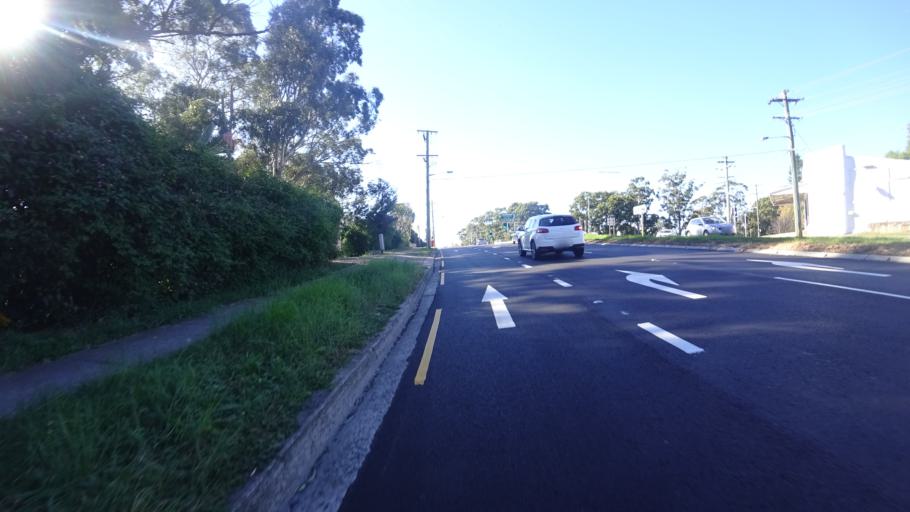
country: AU
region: New South Wales
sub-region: The Hills Shire
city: Castle Hill
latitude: -33.7313
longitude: 151.0162
